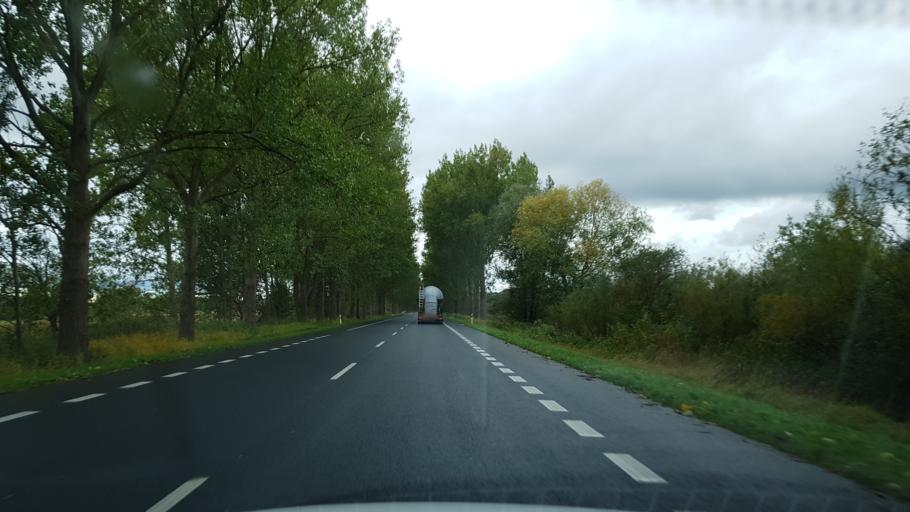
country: PL
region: West Pomeranian Voivodeship
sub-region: Powiat kamienski
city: Wolin
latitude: 53.8509
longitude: 14.5958
